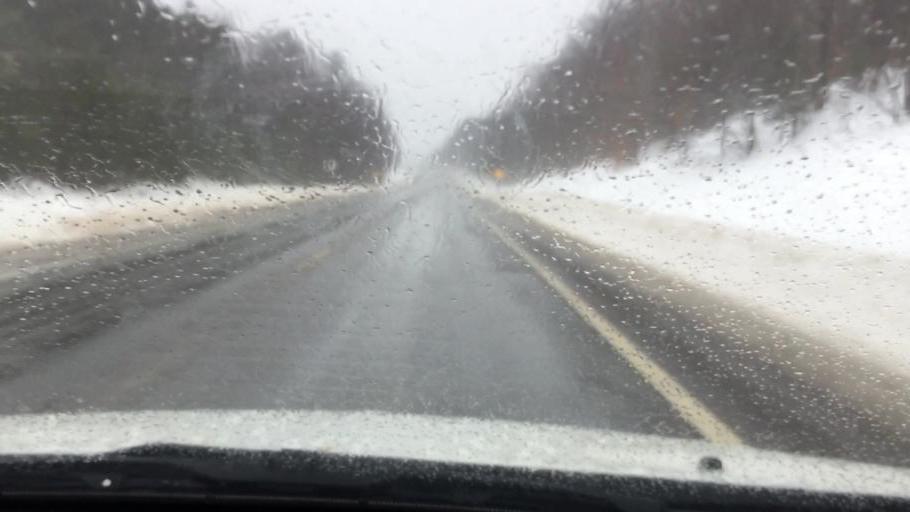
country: US
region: Michigan
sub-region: Antrim County
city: Mancelona
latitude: 44.9778
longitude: -85.0542
